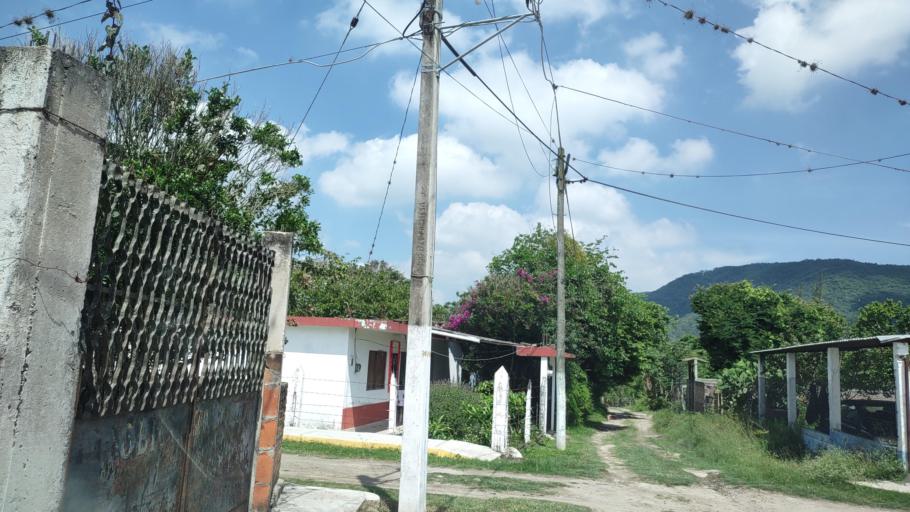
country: MX
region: Veracruz
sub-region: Emiliano Zapata
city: Dos Rios
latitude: 19.4291
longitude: -96.8077
